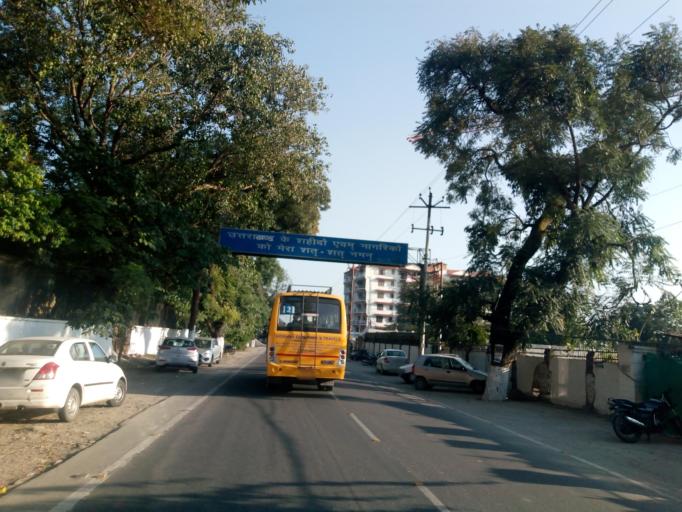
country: IN
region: Uttarakhand
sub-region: Dehradun
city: Dehradun
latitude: 30.3437
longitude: 78.0483
